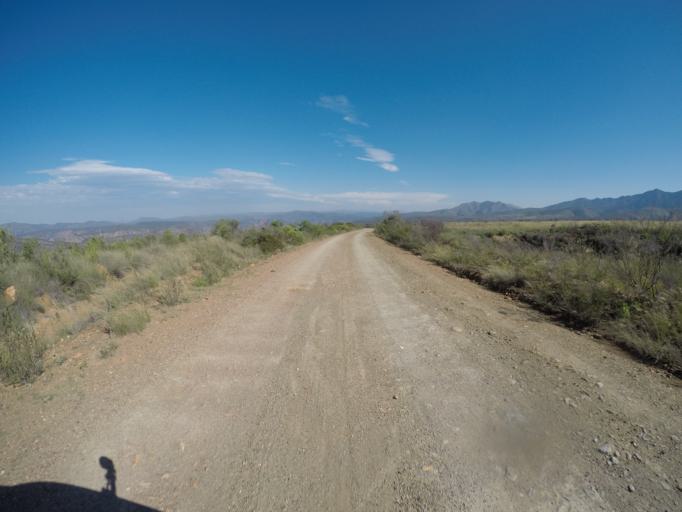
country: ZA
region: Eastern Cape
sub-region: Cacadu District Municipality
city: Kareedouw
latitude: -33.6343
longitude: 24.4770
